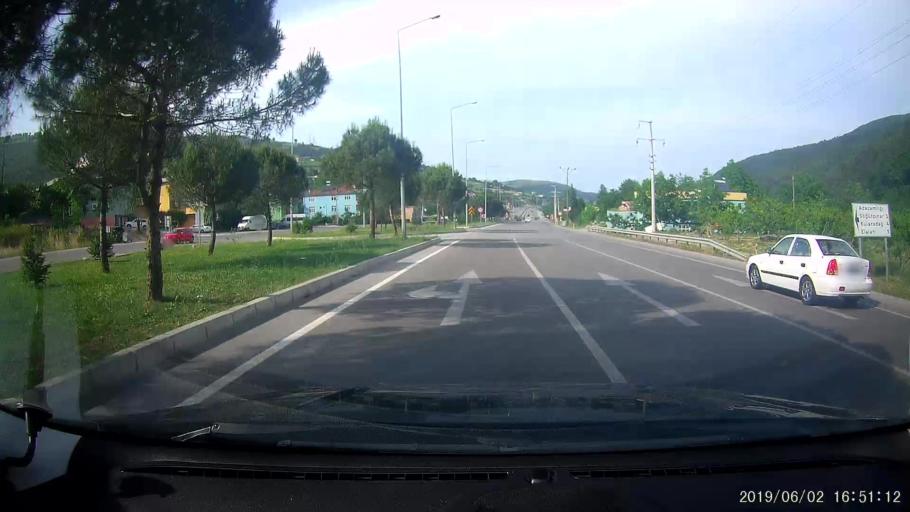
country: TR
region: Samsun
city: Taflan
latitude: 41.2702
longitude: 36.1791
